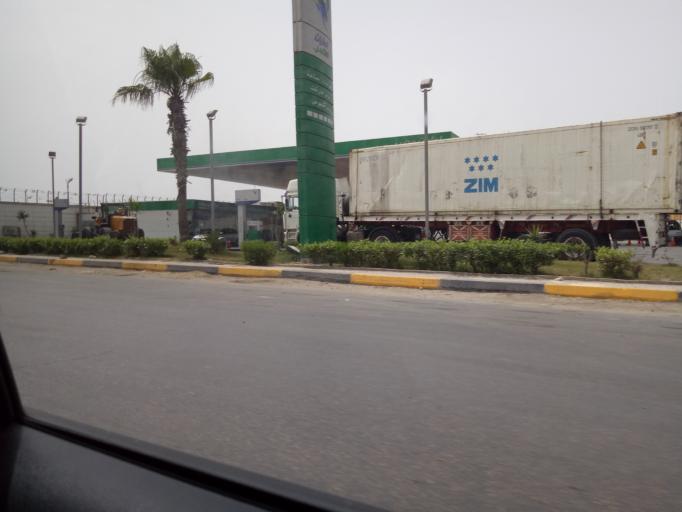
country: EG
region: Alexandria
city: Alexandria
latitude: 31.1449
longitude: 29.8370
